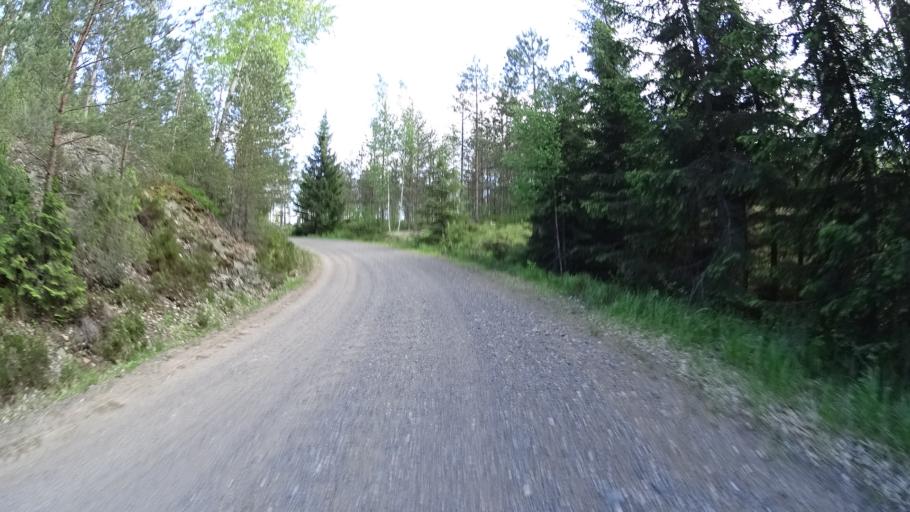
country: FI
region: Uusimaa
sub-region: Raaseporin
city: Pohja
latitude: 60.1567
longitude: 23.4882
